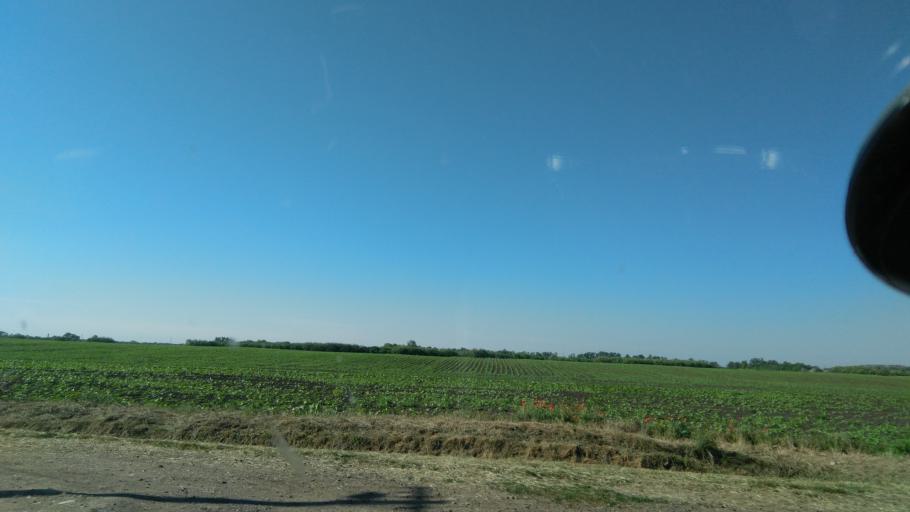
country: HU
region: Bekes
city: Elek
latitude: 46.5292
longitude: 21.2321
